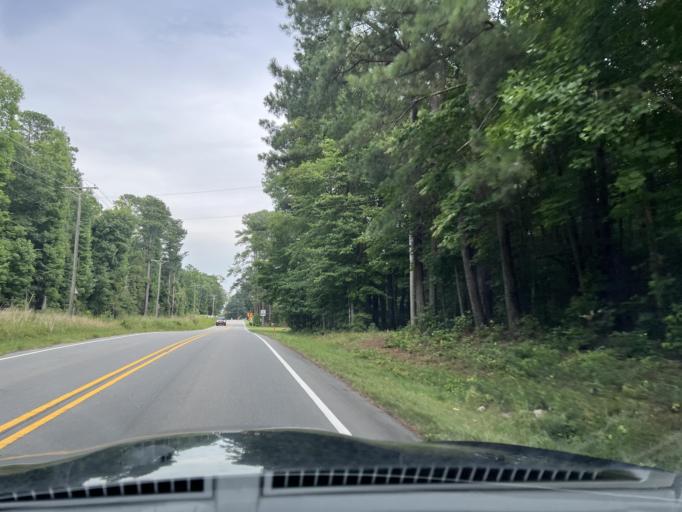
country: US
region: North Carolina
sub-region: Wake County
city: Wake Forest
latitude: 36.0146
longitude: -78.5687
